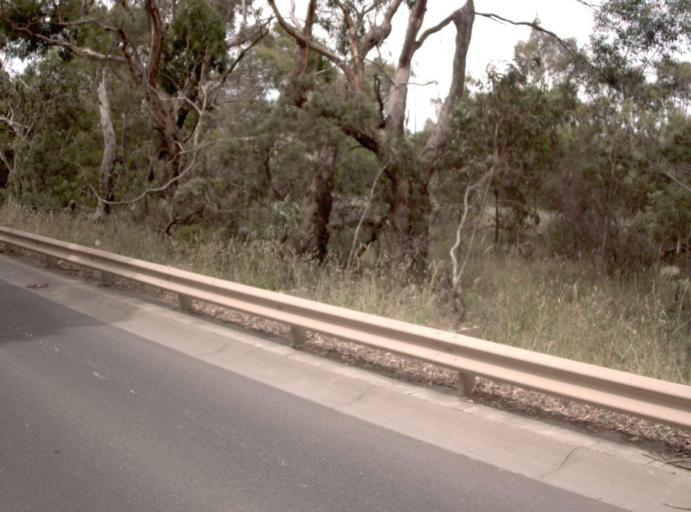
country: AU
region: Victoria
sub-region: Mornington Peninsula
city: Mornington
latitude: -38.2565
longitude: 145.0777
